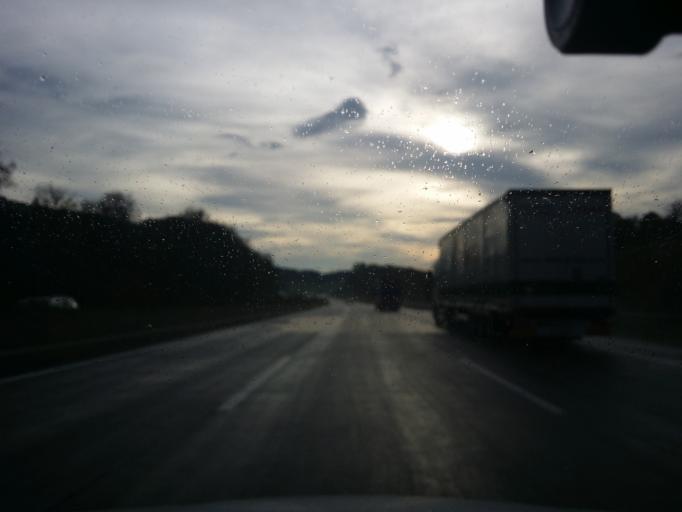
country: DE
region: Thuringia
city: Krauthausen
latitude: 51.0111
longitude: 10.2910
